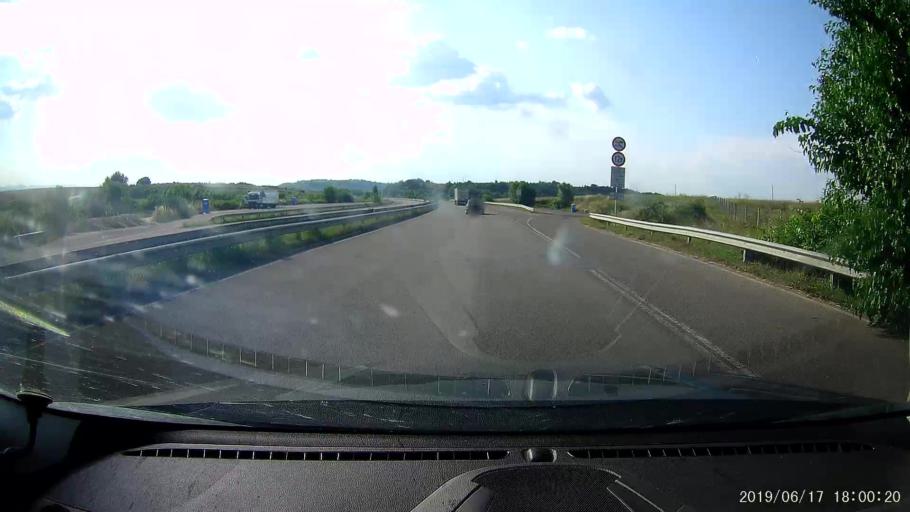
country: BG
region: Khaskovo
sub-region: Obshtina Svilengrad
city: Svilengrad
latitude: 41.7352
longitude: 26.2811
